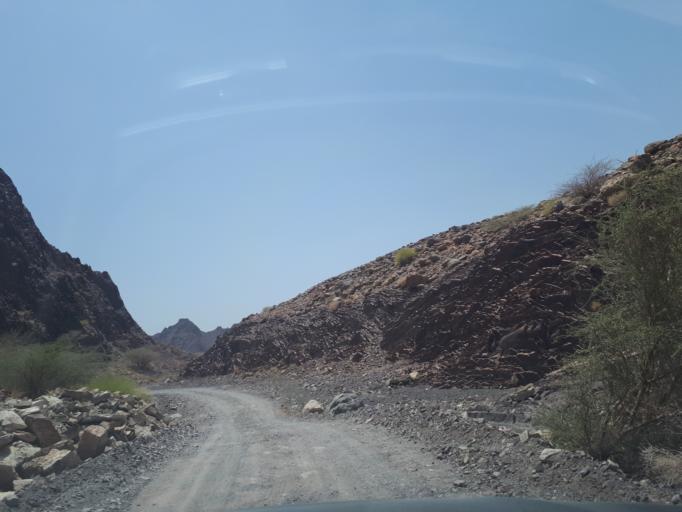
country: OM
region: Ash Sharqiyah
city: Badiyah
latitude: 22.4904
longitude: 59.1279
